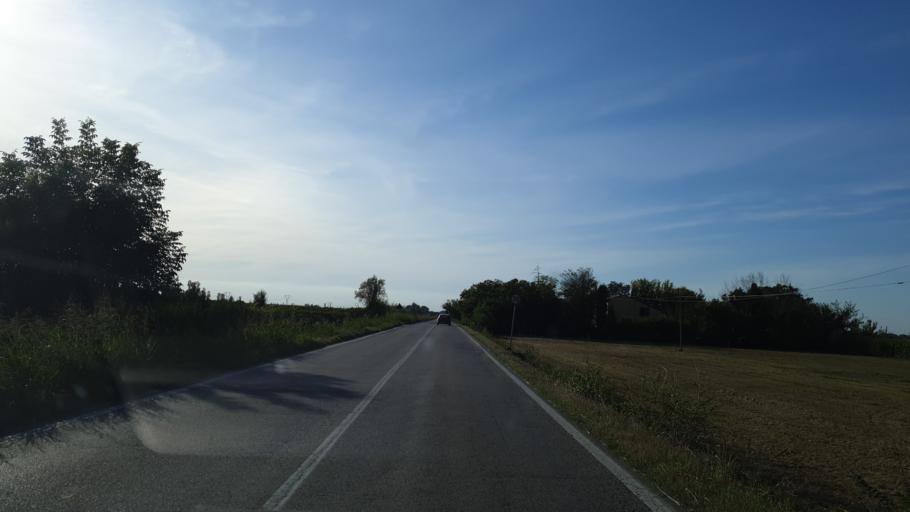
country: IT
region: Emilia-Romagna
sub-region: Provincia di Ravenna
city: Voltana
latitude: 44.5450
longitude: 11.9761
